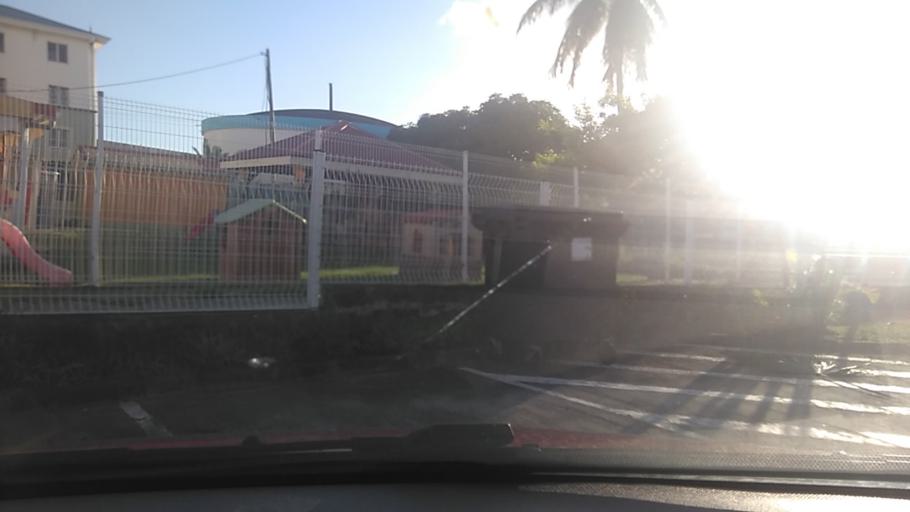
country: MQ
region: Martinique
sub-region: Martinique
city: Fort-de-France
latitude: 14.6044
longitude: -61.0917
